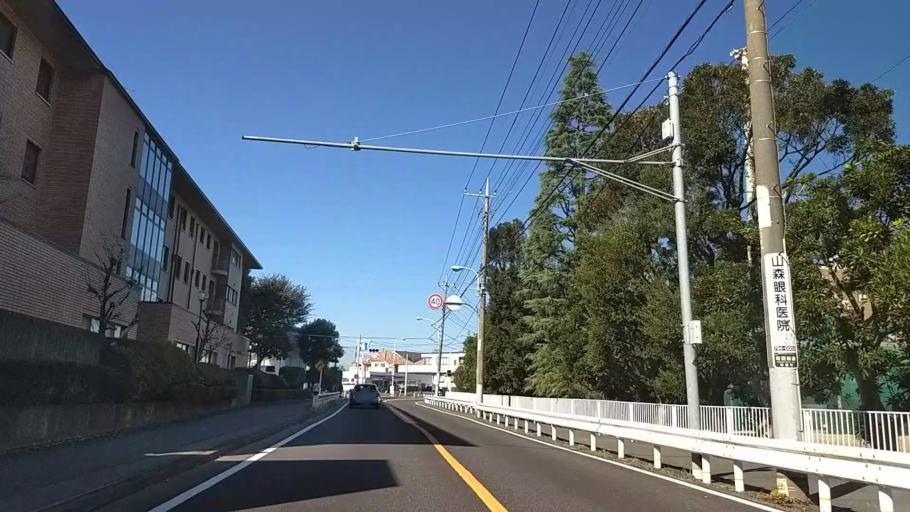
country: JP
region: Tokyo
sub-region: Machida-shi
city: Machida
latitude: 35.5807
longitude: 139.4056
